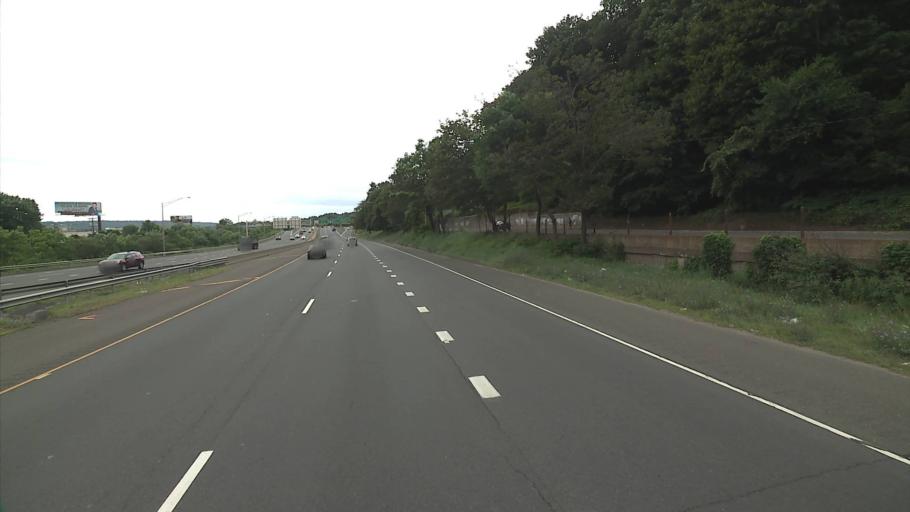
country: US
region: Connecticut
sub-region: New Haven County
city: Waterbury
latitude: 41.5630
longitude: -73.0581
